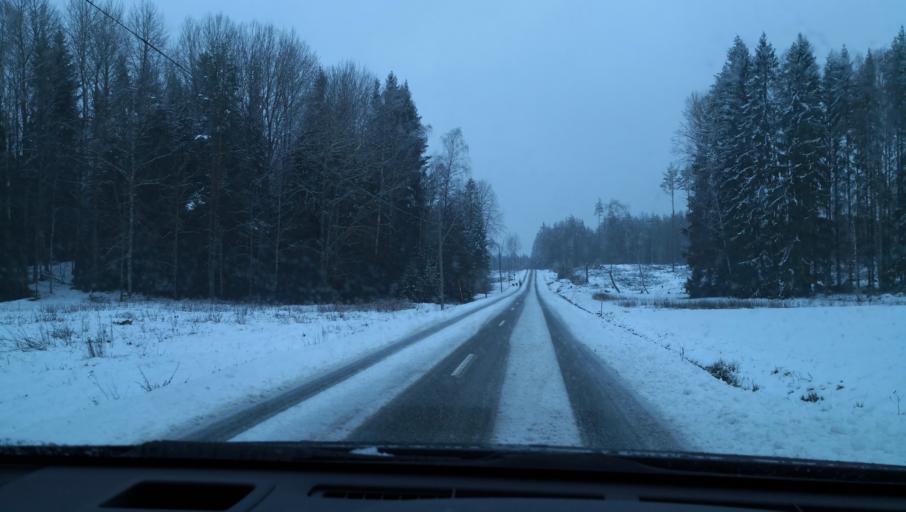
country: SE
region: Vaestmanland
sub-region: Kopings Kommun
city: Kolsva
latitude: 59.5883
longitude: 15.8084
